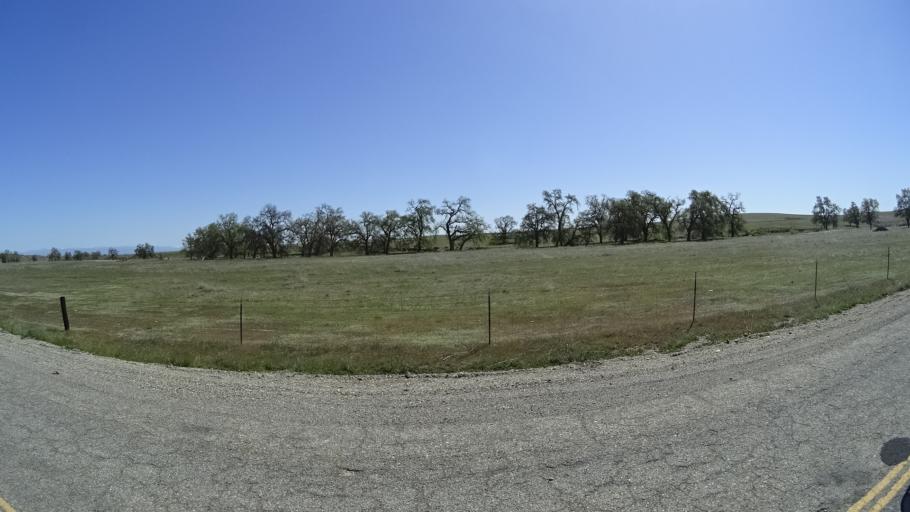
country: US
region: California
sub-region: Glenn County
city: Orland
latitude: 39.7728
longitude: -122.3223
